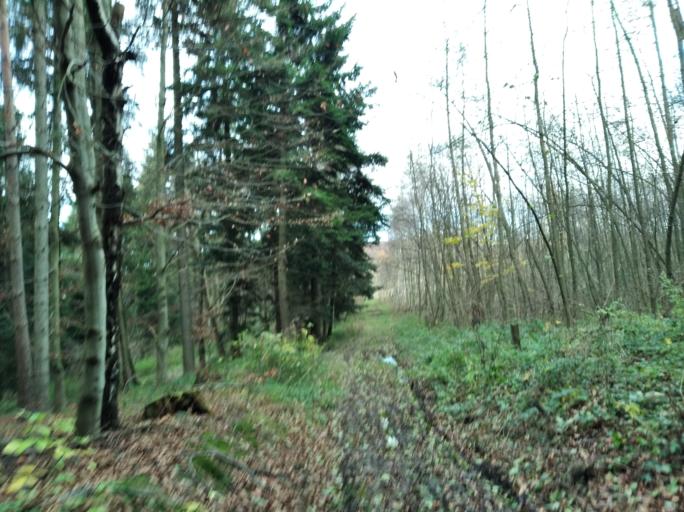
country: PL
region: Subcarpathian Voivodeship
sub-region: Powiat strzyzowski
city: Jawornik
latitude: 49.8652
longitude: 21.8559
